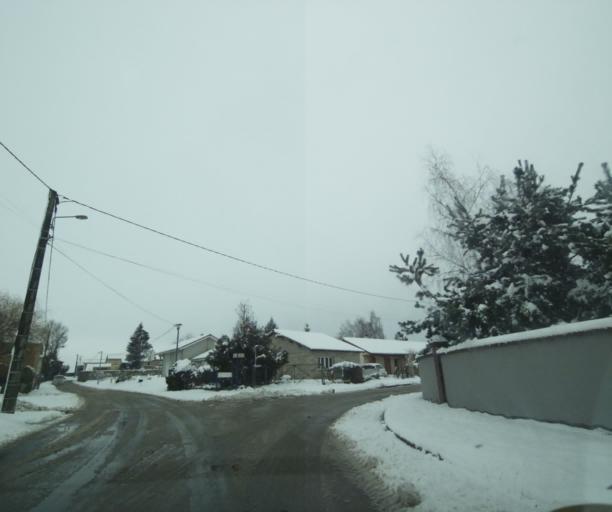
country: FR
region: Champagne-Ardenne
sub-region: Departement de la Haute-Marne
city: Montier-en-Der
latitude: 48.5064
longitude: 4.7867
